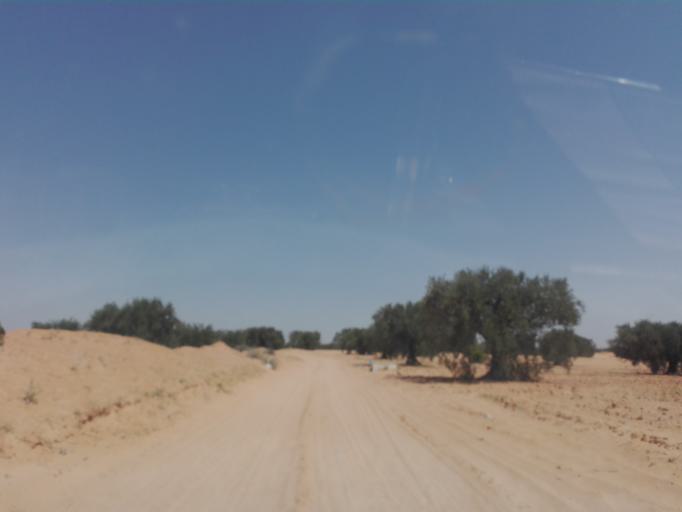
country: TN
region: Safaqis
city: Bi'r `Ali Bin Khalifah
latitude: 34.6481
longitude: 10.2517
